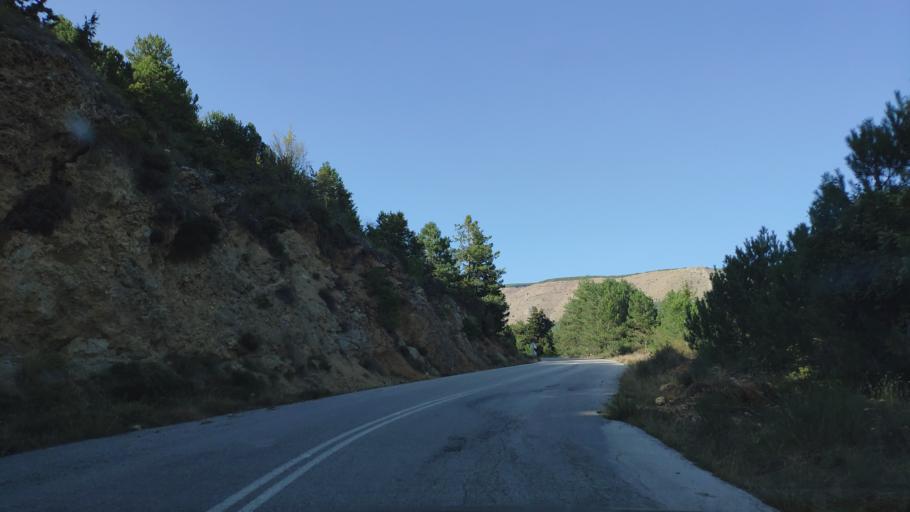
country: GR
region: West Greece
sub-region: Nomos Achaias
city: Aiyira
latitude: 38.0162
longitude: 22.4044
